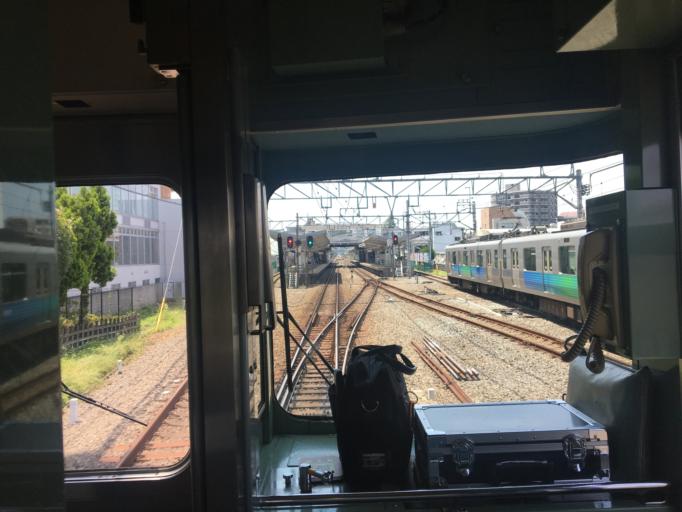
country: JP
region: Tokyo
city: Tanashicho
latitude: 35.7716
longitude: 139.5215
